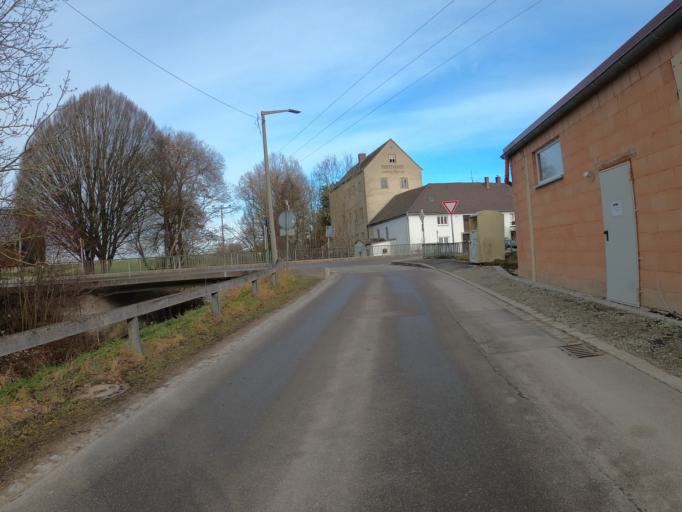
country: DE
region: Bavaria
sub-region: Swabia
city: Leipheim
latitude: 48.4208
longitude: 10.1815
